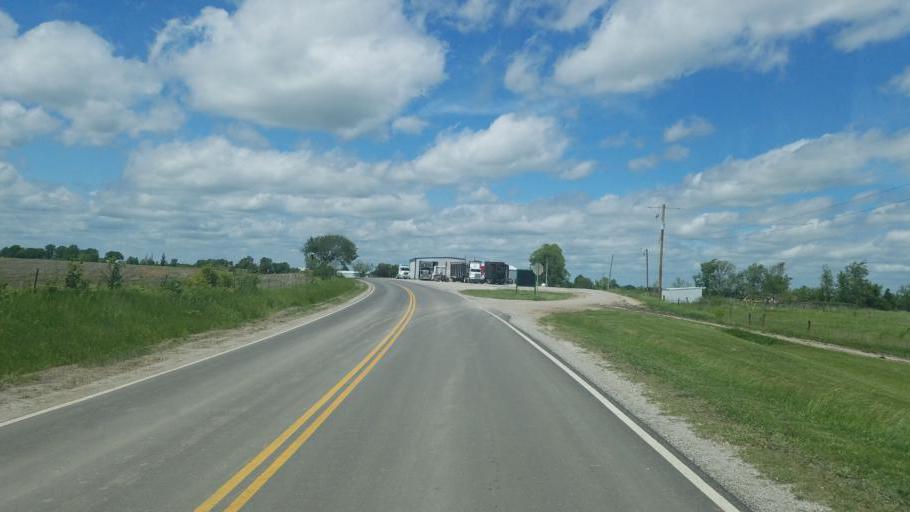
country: US
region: Iowa
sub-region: Decatur County
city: Lamoni
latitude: 40.4758
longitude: -93.9889
